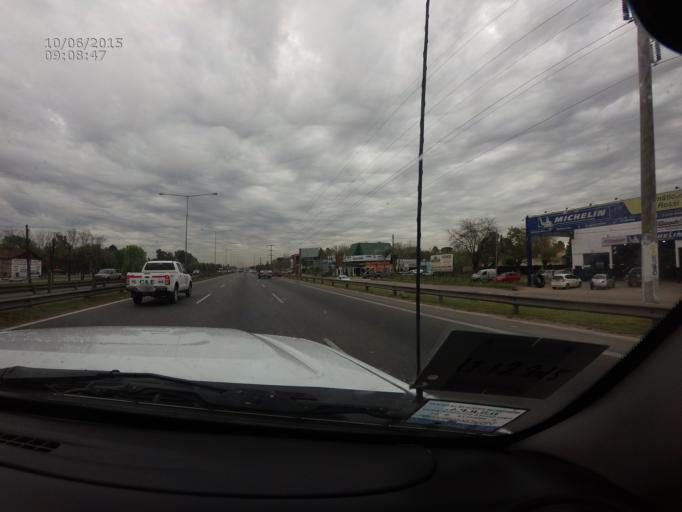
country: AR
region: Buenos Aires
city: Santa Catalina - Dique Lujan
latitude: -34.3855
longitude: -58.7474
